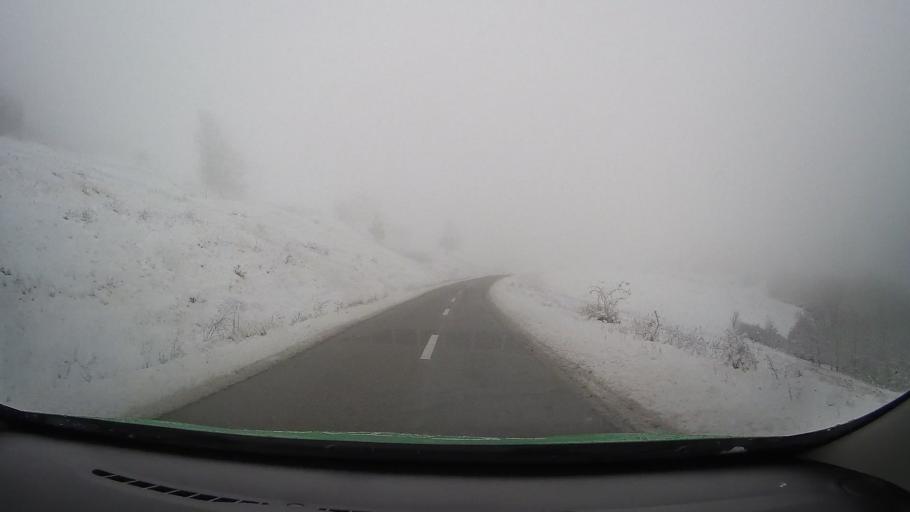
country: RO
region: Hunedoara
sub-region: Comuna Teliucu Inferior
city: Teliucu Inferior
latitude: 45.6677
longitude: 22.9179
